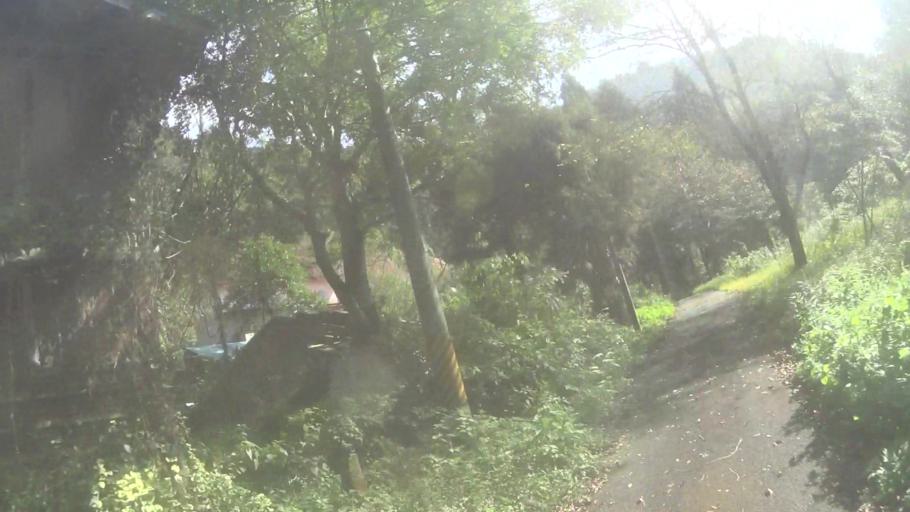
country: JP
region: Kyoto
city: Miyazu
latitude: 35.7154
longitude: 135.1662
